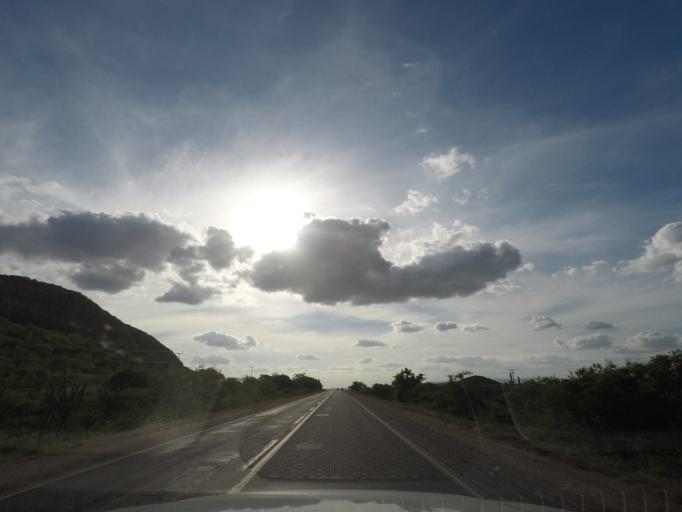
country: BR
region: Bahia
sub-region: Anguera
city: Anguera
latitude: -12.1825
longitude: -39.4628
